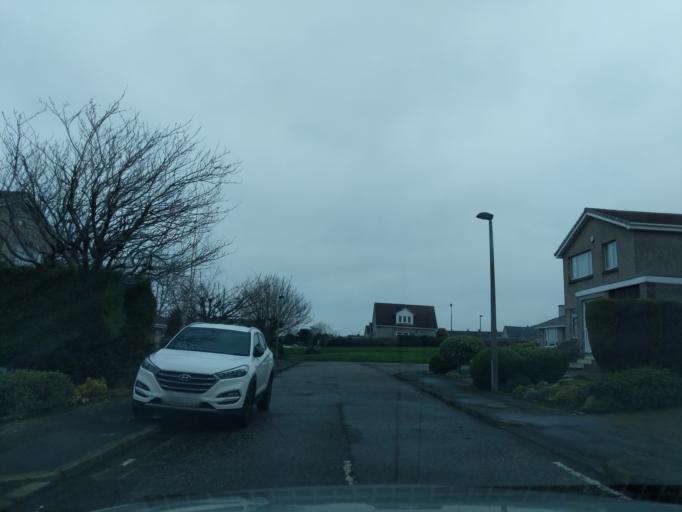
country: GB
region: Scotland
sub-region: Edinburgh
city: Balerno
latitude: 55.8931
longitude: -3.3274
